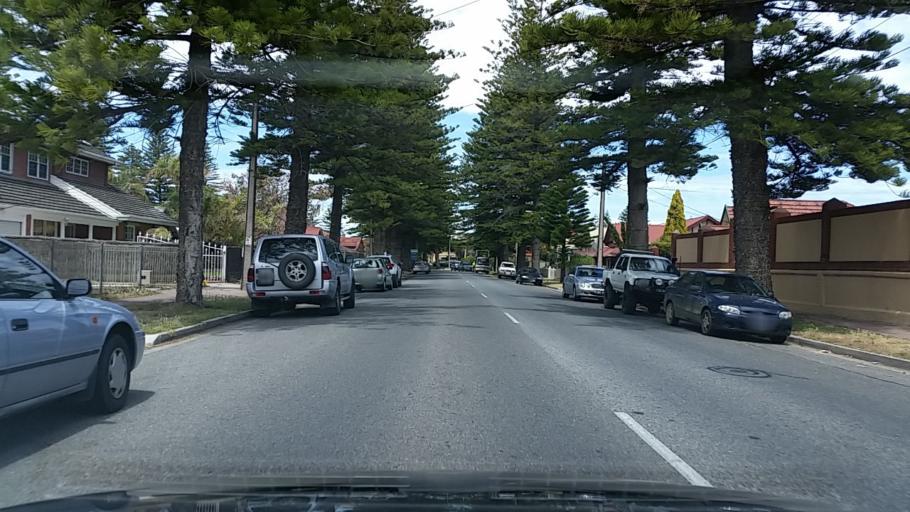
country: AU
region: South Australia
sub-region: Charles Sturt
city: Henley Beach
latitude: -34.9236
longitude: 138.4967
